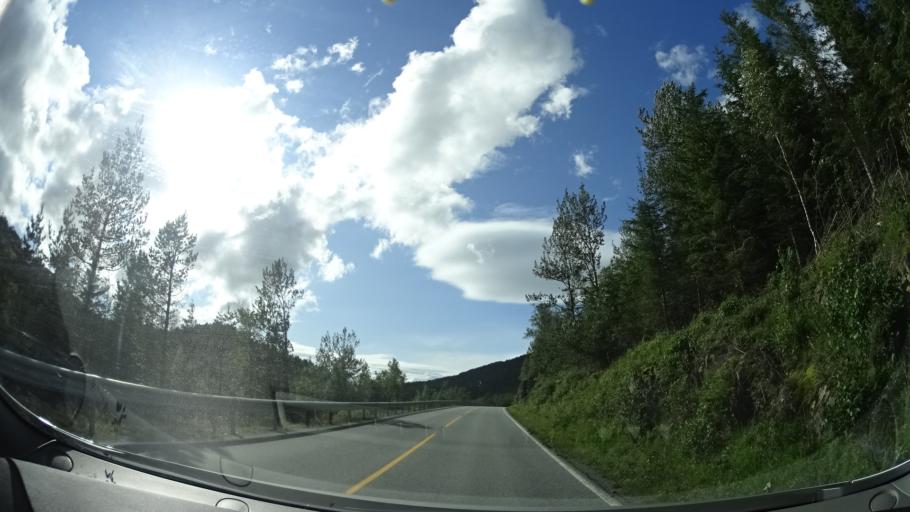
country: NO
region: Sor-Trondelag
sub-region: Hemne
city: Kyrksaeterora
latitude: 63.2130
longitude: 9.1341
